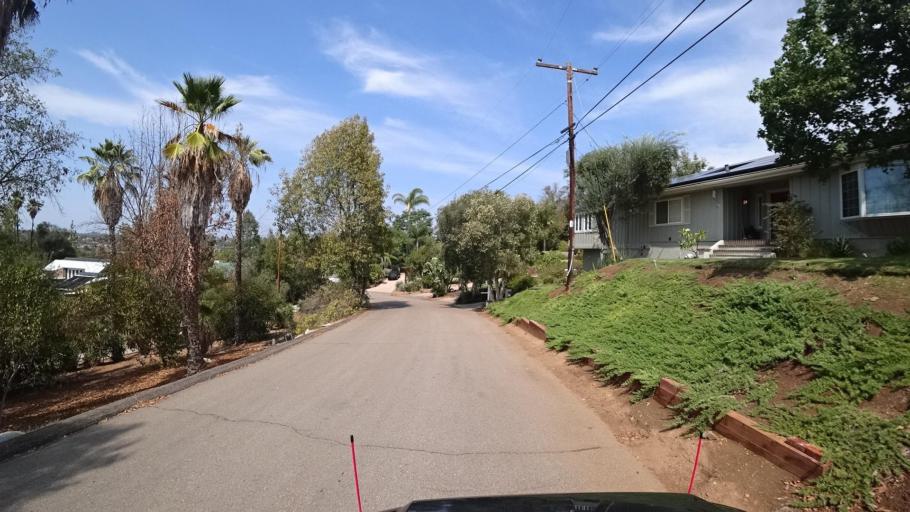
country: US
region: California
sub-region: San Diego County
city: Escondido
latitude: 33.0837
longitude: -117.0483
